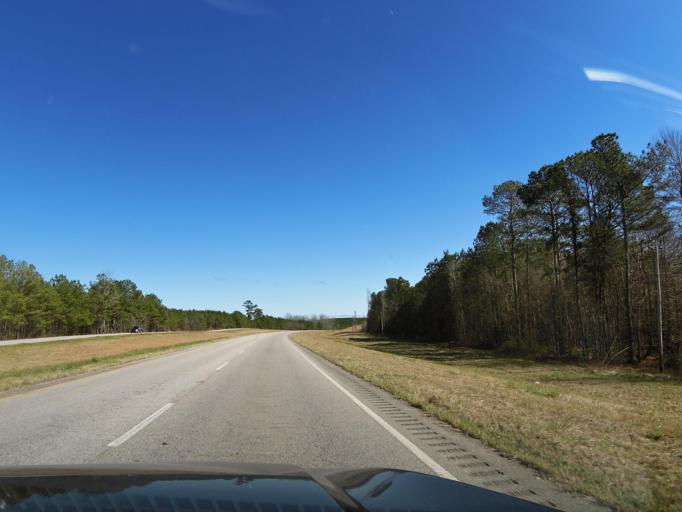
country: US
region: Alabama
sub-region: Bullock County
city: Union Springs
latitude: 32.1462
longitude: -85.6292
